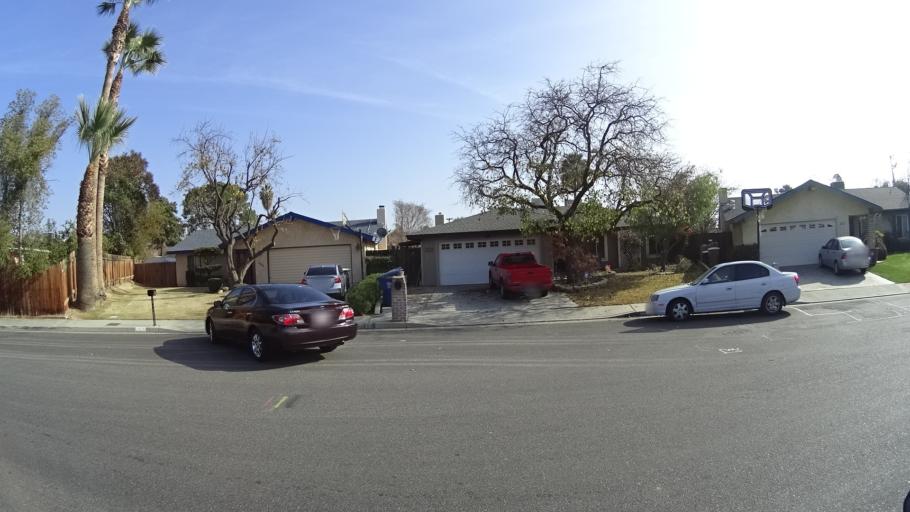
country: US
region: California
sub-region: Kern County
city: Bakersfield
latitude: 35.3872
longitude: -118.9595
